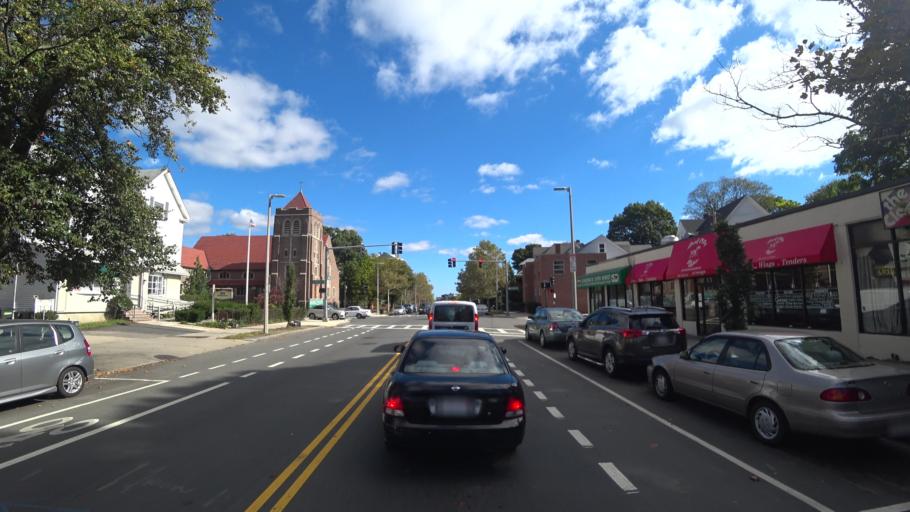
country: US
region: Massachusetts
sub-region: Norfolk County
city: Brookline
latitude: 42.3523
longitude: -71.1407
